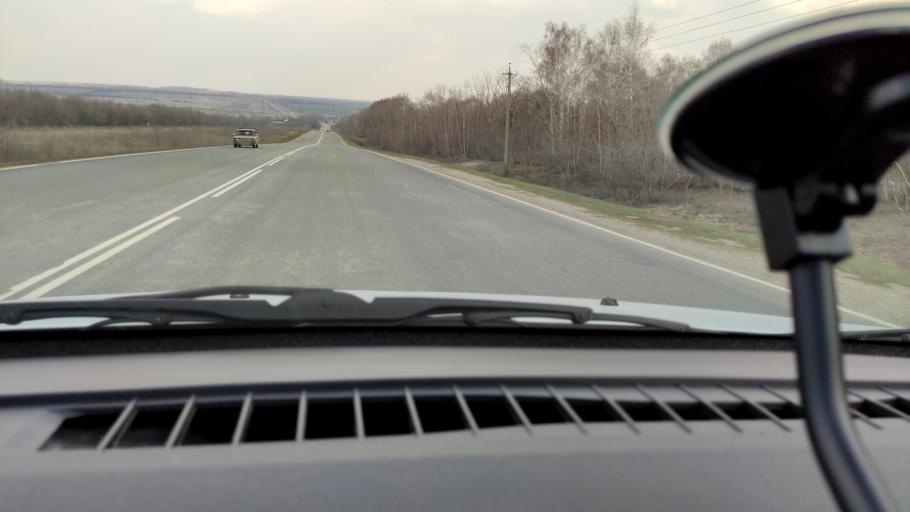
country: RU
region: Samara
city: Dubovyy Umet
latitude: 53.0752
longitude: 50.3553
